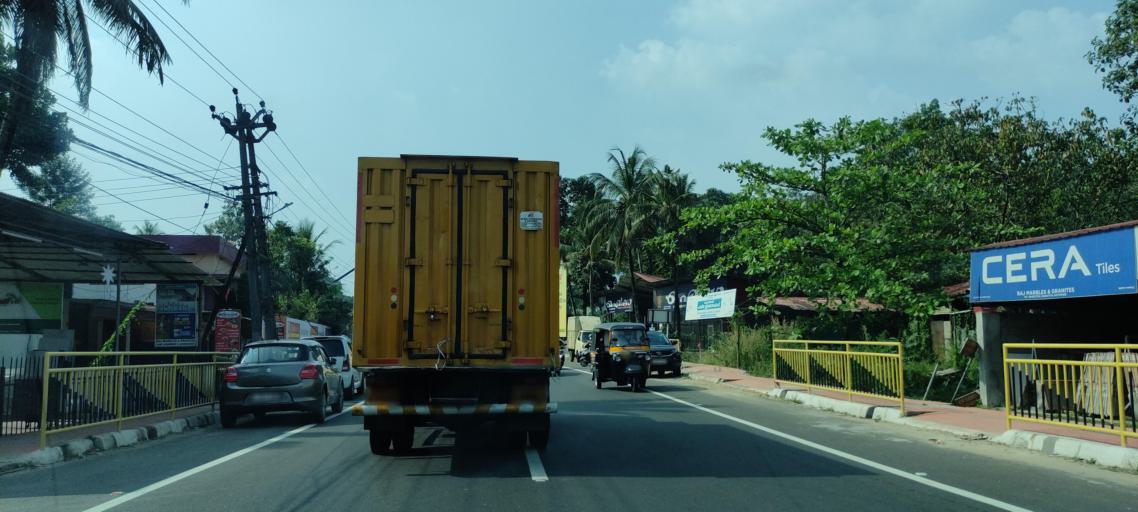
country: IN
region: Kerala
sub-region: Alappuzha
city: Chengannur
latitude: 9.2923
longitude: 76.6461
